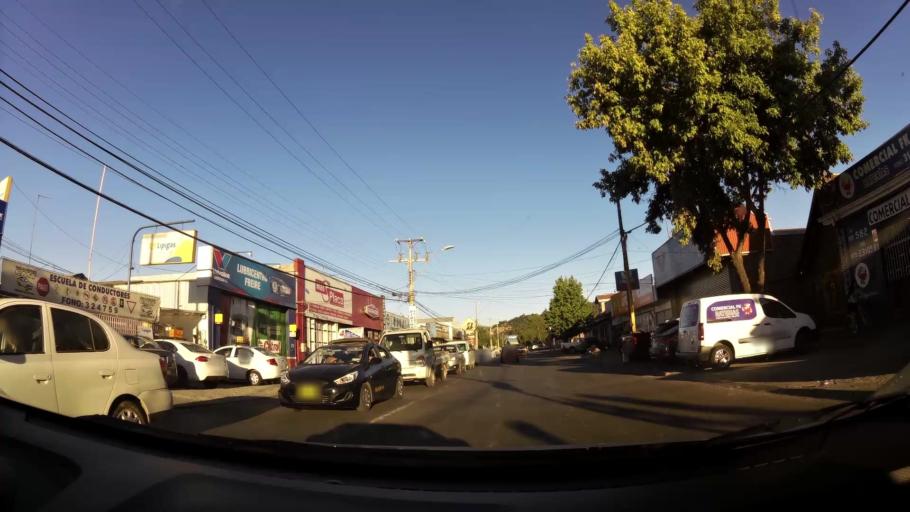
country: CL
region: Maule
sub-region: Provincia de Curico
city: Curico
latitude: -34.9767
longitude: -71.2434
